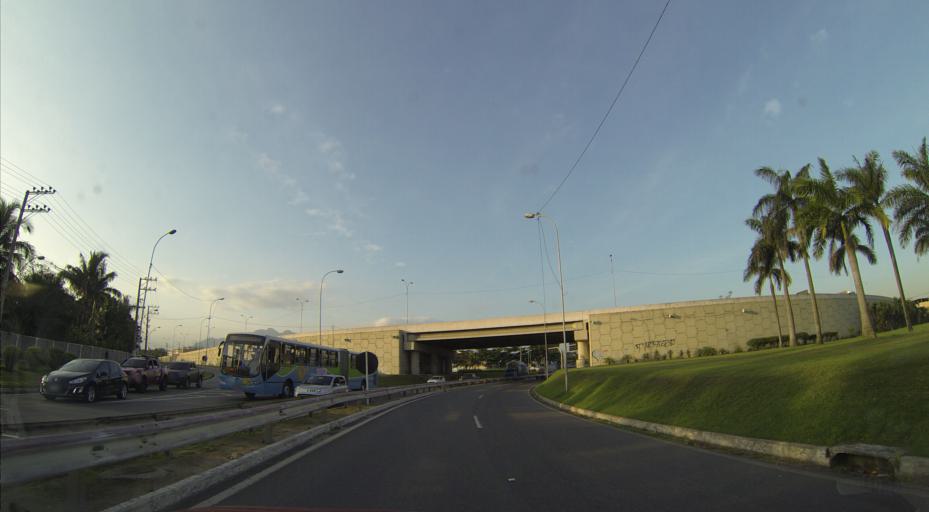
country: BR
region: Espirito Santo
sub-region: Vila Velha
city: Vila Velha
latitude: -20.2339
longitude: -40.2757
